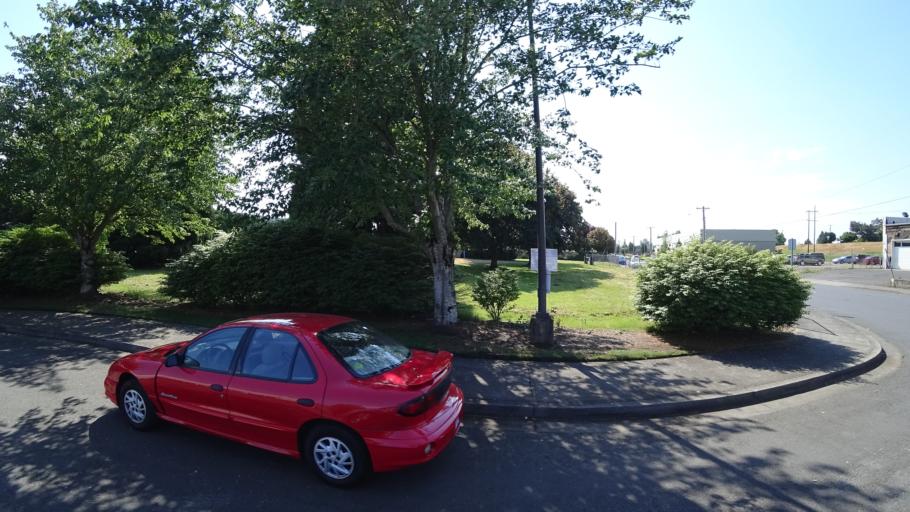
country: US
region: Washington
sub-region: Clark County
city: Mill Plain
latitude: 45.5640
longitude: -122.5179
